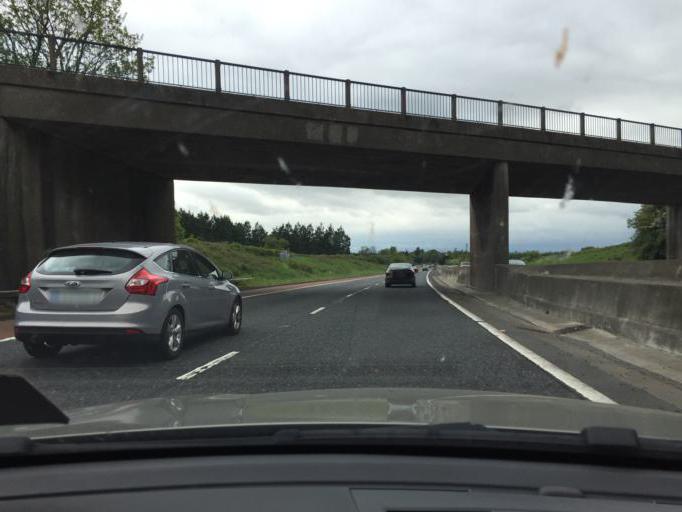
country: GB
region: Northern Ireland
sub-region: Lisburn District
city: Lisburn
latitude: 54.5131
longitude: -6.0140
